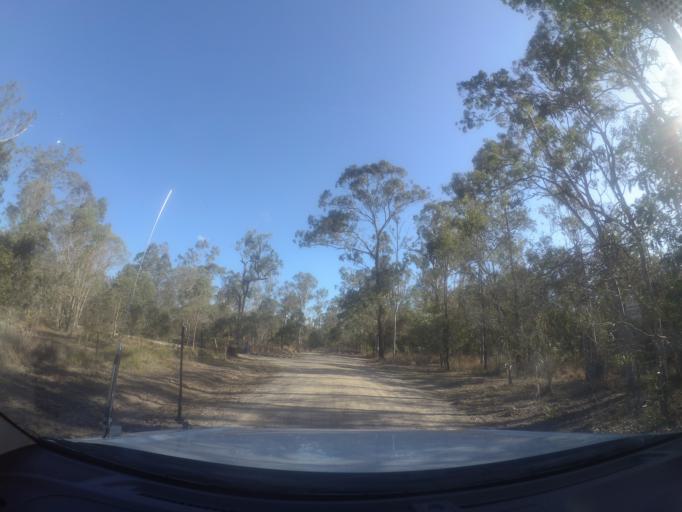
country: AU
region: Queensland
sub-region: Logan
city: Park Ridge South
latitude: -27.7344
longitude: 153.0541
